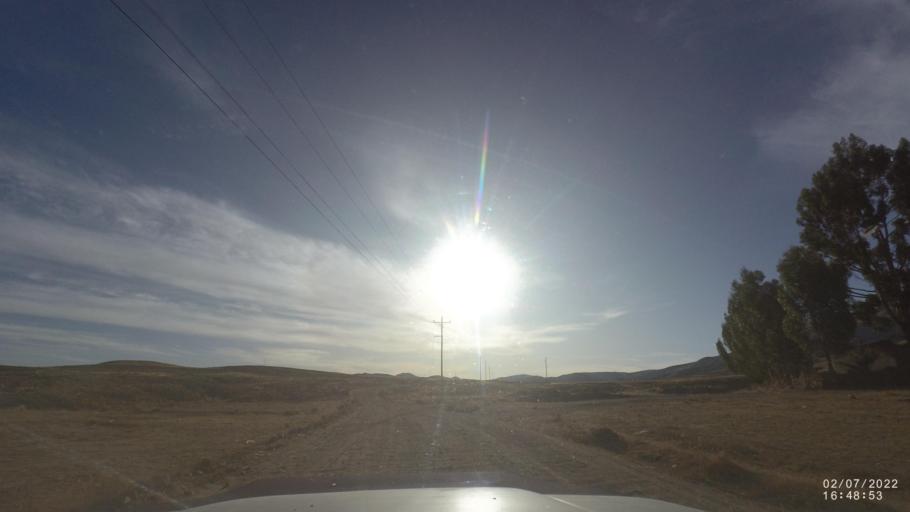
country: BO
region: Cochabamba
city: Irpa Irpa
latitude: -17.9762
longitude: -66.5229
